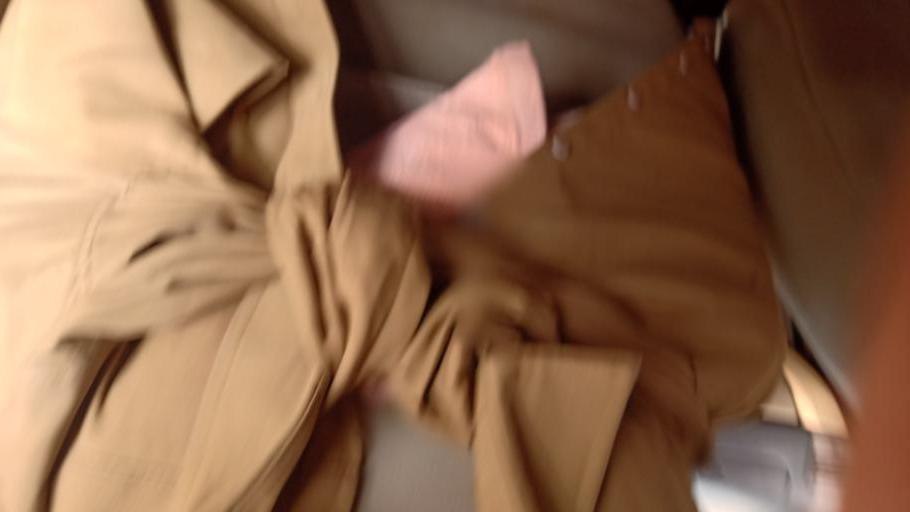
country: IN
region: Telangana
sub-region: Rangareddi
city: Kukatpalli
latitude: 17.4981
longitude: 78.4147
